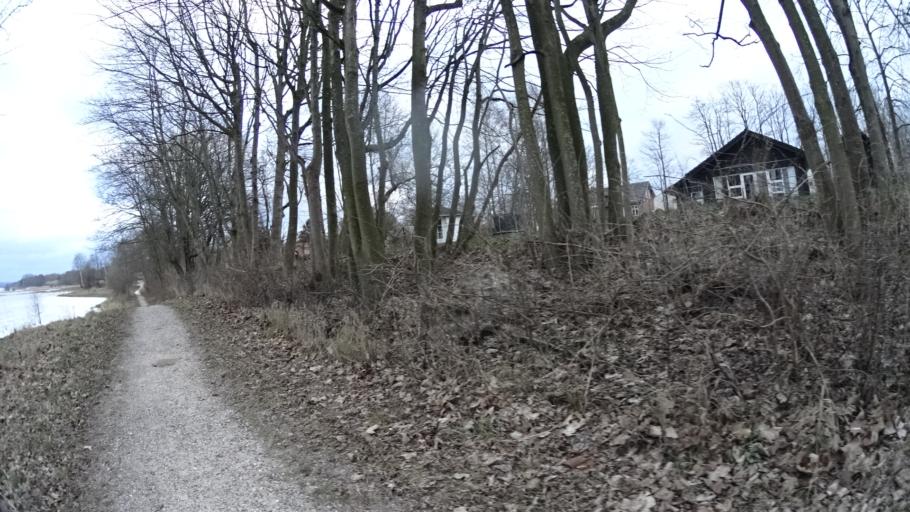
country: DK
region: Central Jutland
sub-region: Arhus Kommune
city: Kolt
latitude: 56.1275
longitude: 10.0481
